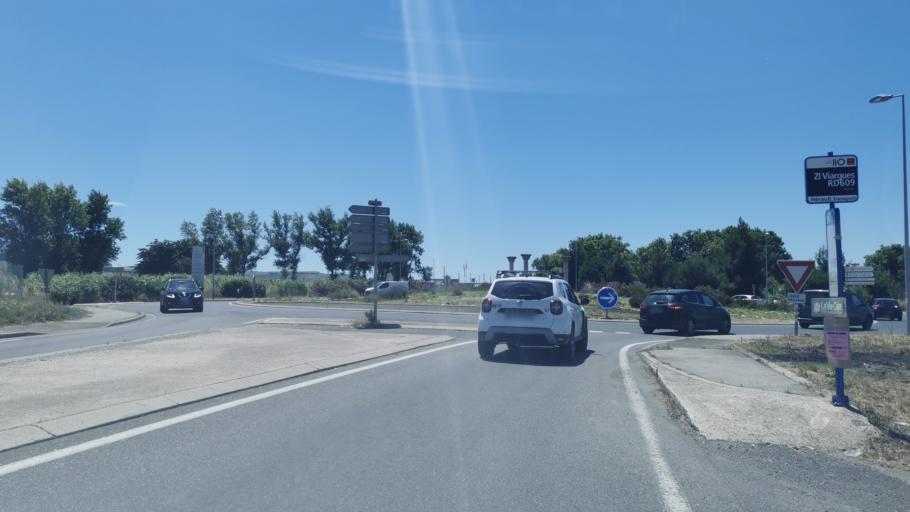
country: FR
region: Languedoc-Roussillon
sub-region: Departement de l'Herault
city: Colombiers
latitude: 43.3085
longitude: 3.1684
